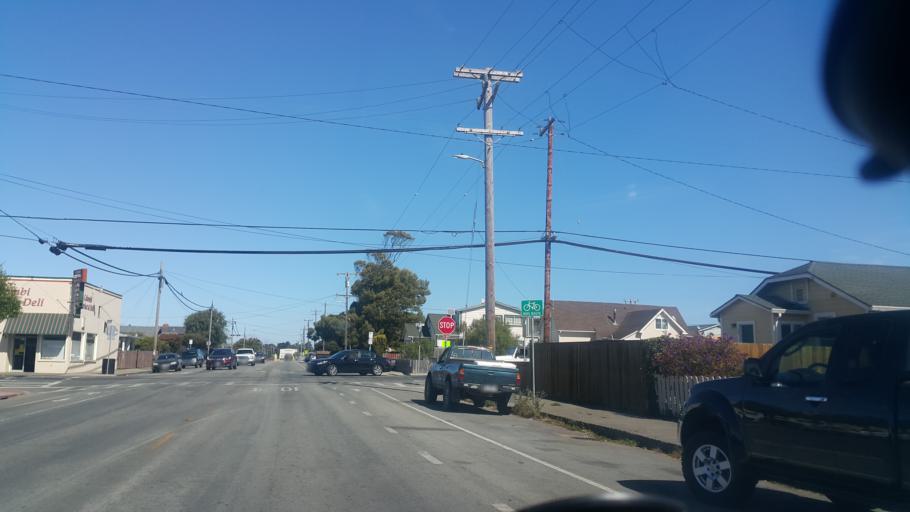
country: US
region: California
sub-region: Mendocino County
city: Fort Bragg
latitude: 39.4412
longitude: -123.7980
